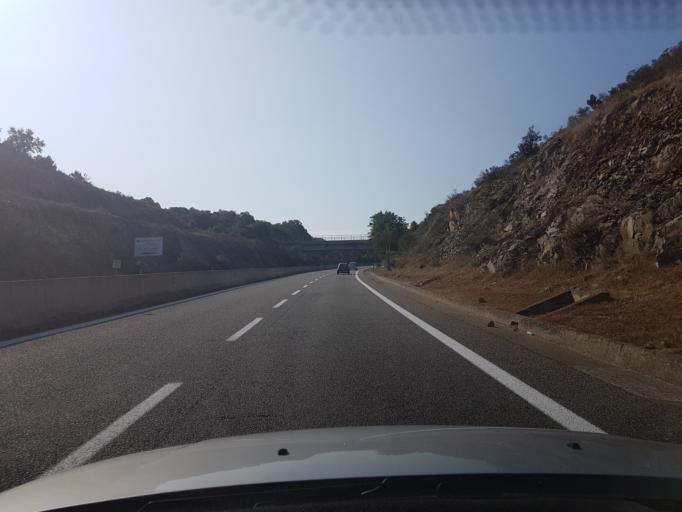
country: IT
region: Sardinia
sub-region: Provincia di Olbia-Tempio
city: Padru
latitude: 40.8113
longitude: 9.5887
